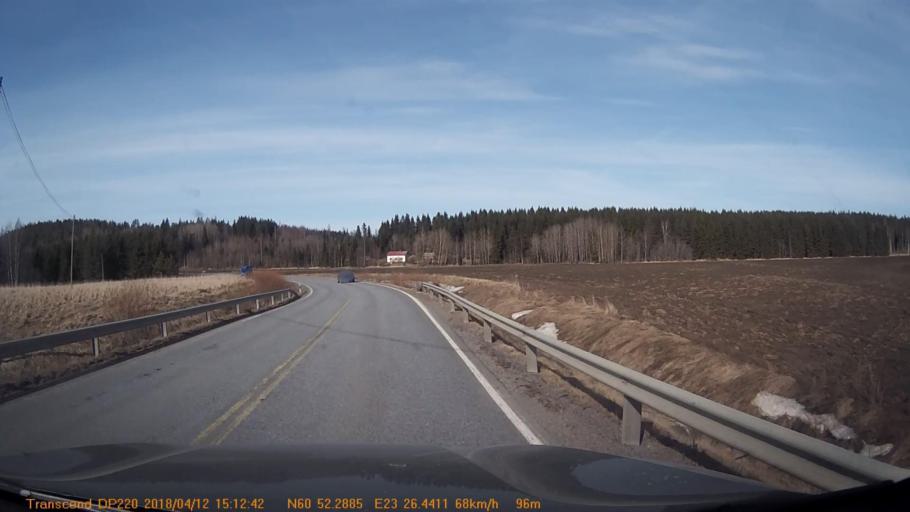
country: FI
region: Haeme
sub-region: Forssa
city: Jokioinen
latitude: 60.8715
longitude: 23.4408
